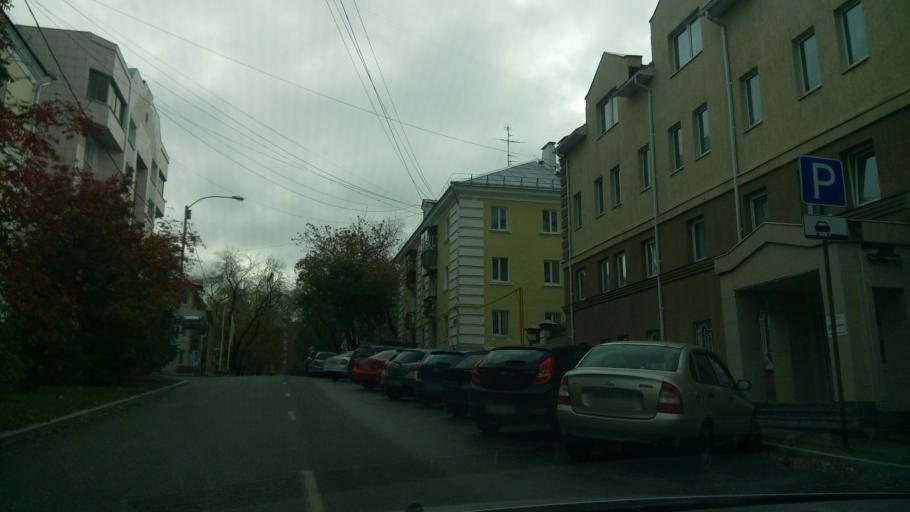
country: RU
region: Sverdlovsk
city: Yekaterinburg
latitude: 56.8417
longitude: 60.5753
